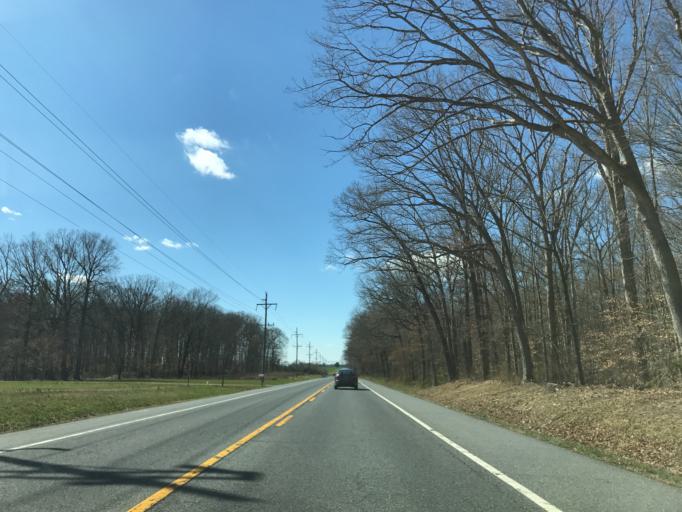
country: US
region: Maryland
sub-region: Queen Anne's County
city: Kingstown
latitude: 39.2632
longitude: -75.9018
